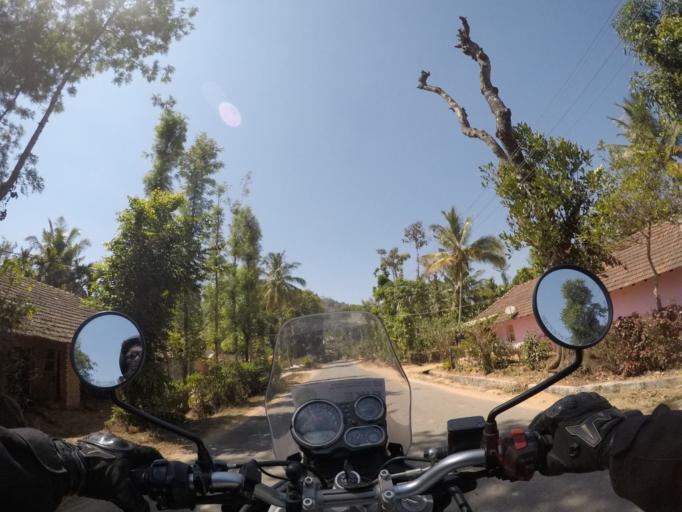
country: IN
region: Karnataka
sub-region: Chikmagalur
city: Mudigere
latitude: 13.0461
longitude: 75.6835
